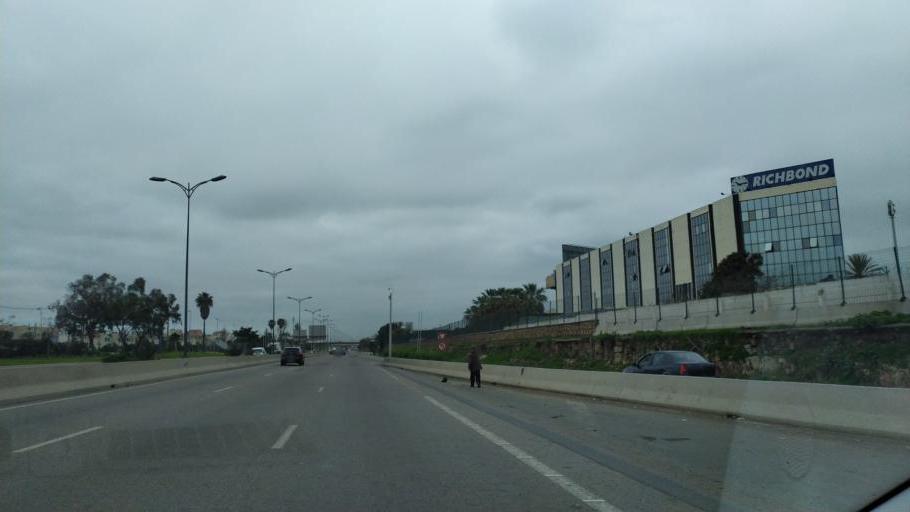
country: MA
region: Grand Casablanca
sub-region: Mediouna
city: Tit Mellil
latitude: 33.6022
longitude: -7.5053
